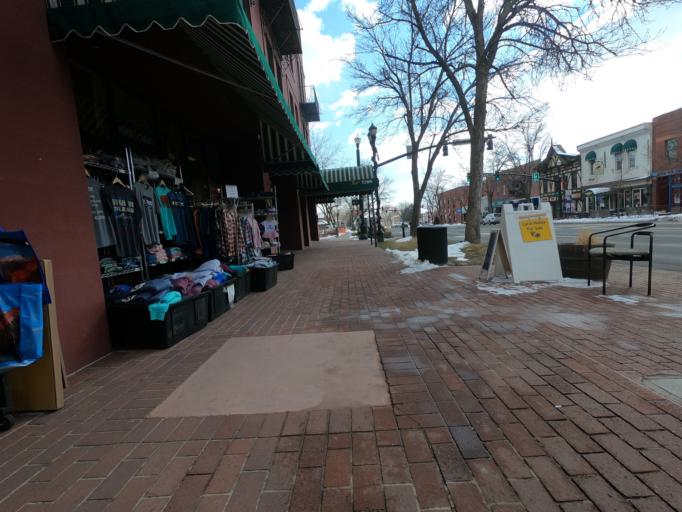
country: US
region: Colorado
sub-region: El Paso County
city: Colorado Springs
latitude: 38.8470
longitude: -104.8622
